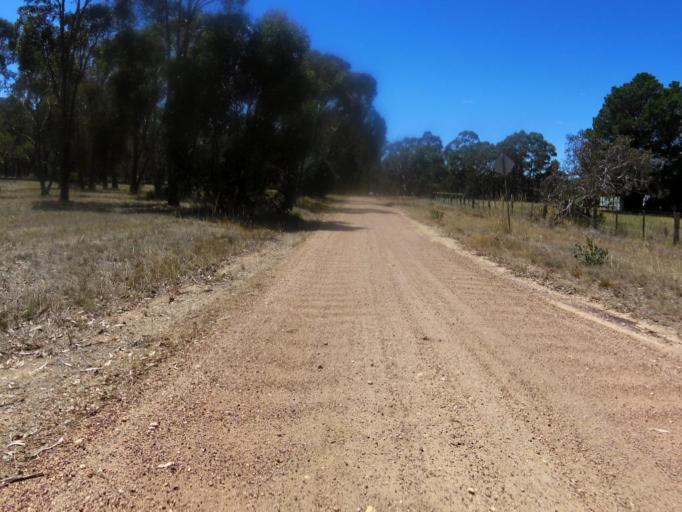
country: AU
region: Victoria
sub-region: Mount Alexander
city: Castlemaine
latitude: -36.9912
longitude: 144.0838
